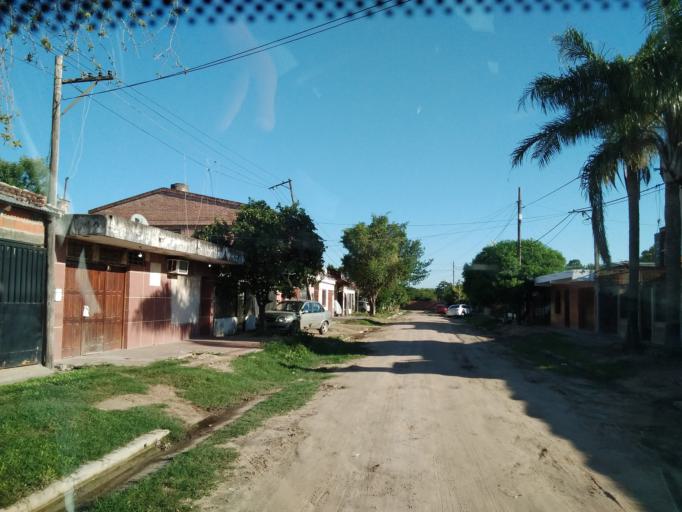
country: AR
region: Corrientes
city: Corrientes
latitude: -27.5065
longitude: -58.7807
